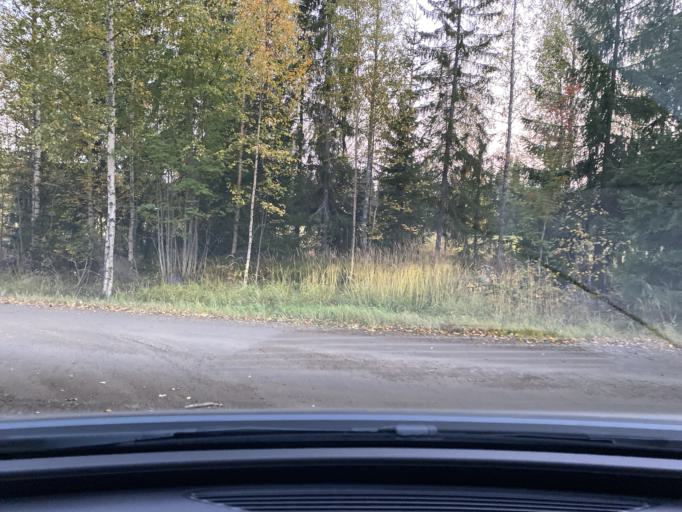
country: FI
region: Pirkanmaa
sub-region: Lounais-Pirkanmaa
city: Punkalaidun
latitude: 61.1154
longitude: 23.2538
